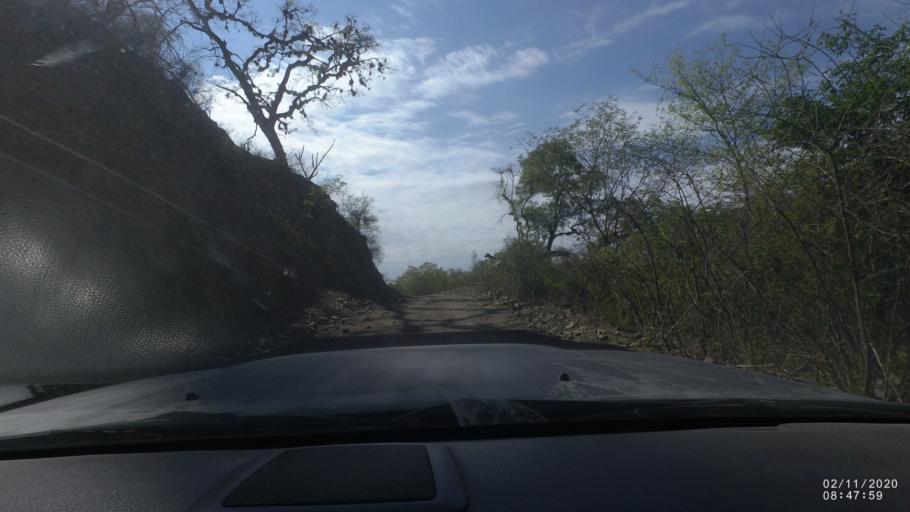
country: BO
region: Chuquisaca
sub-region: Provincia Zudanez
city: Mojocoya
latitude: -18.5598
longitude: -64.5474
